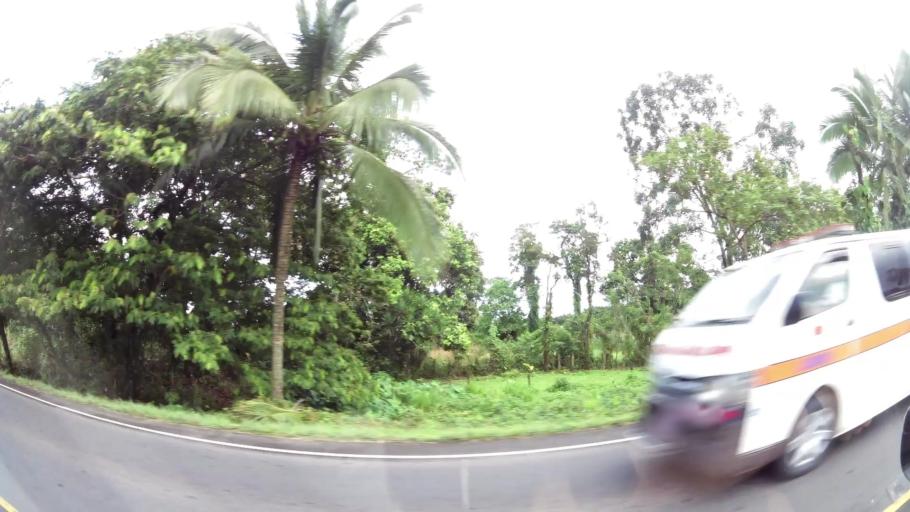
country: CR
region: Limon
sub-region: Canton de Pococi
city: Guapiles
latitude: 10.2023
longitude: -83.7977
